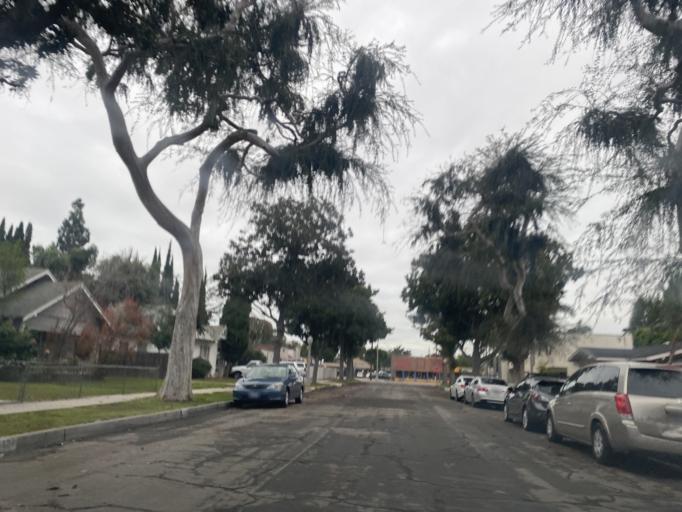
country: US
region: California
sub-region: Orange County
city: Fullerton
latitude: 33.8713
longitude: -117.9130
